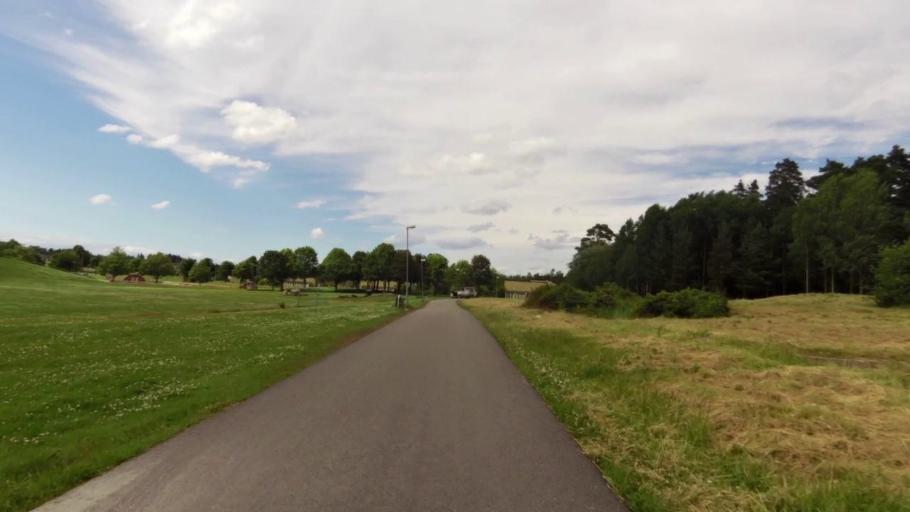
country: SE
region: OEstergoetland
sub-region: Linkopings Kommun
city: Linkoping
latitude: 58.4104
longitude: 15.5730
